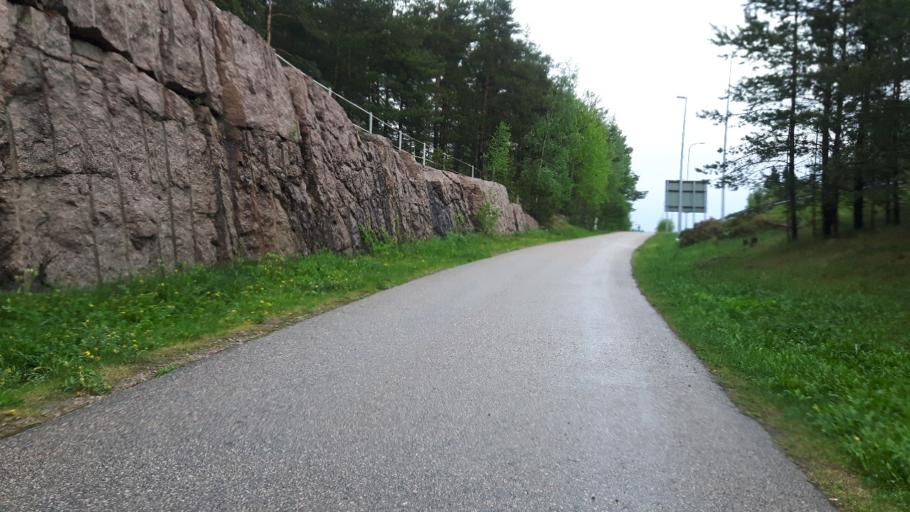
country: FI
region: Kymenlaakso
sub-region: Kotka-Hamina
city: Karhula
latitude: 60.5337
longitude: 26.9565
